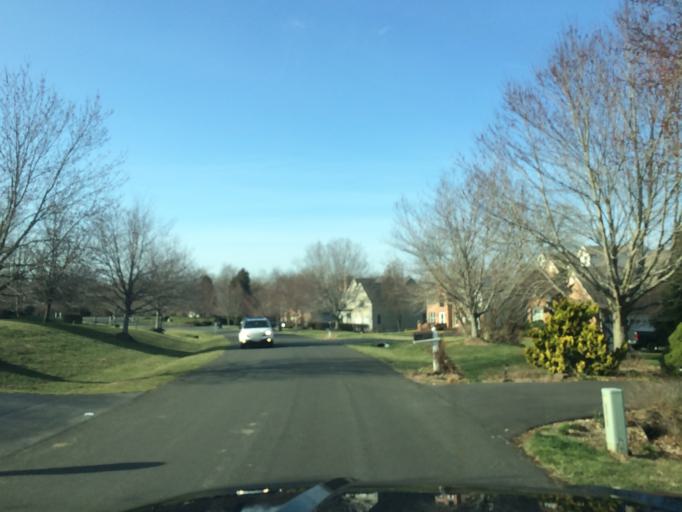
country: US
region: Maryland
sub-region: Carroll County
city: Sykesville
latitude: 39.2876
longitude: -76.9715
